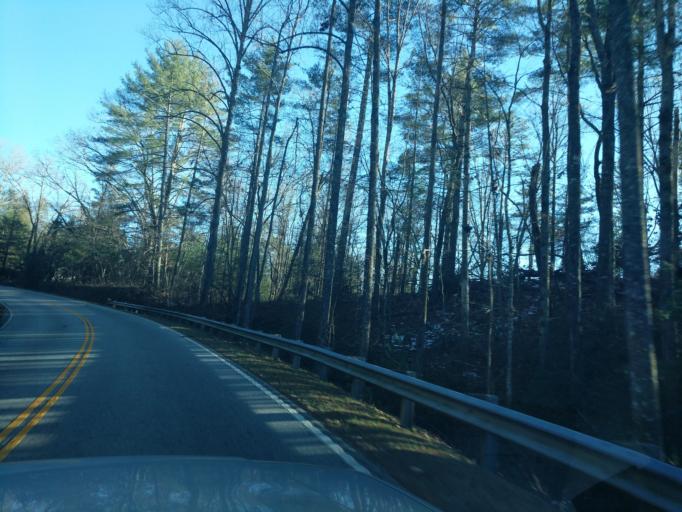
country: US
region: Georgia
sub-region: Rabun County
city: Clayton
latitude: 34.8111
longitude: -83.2879
